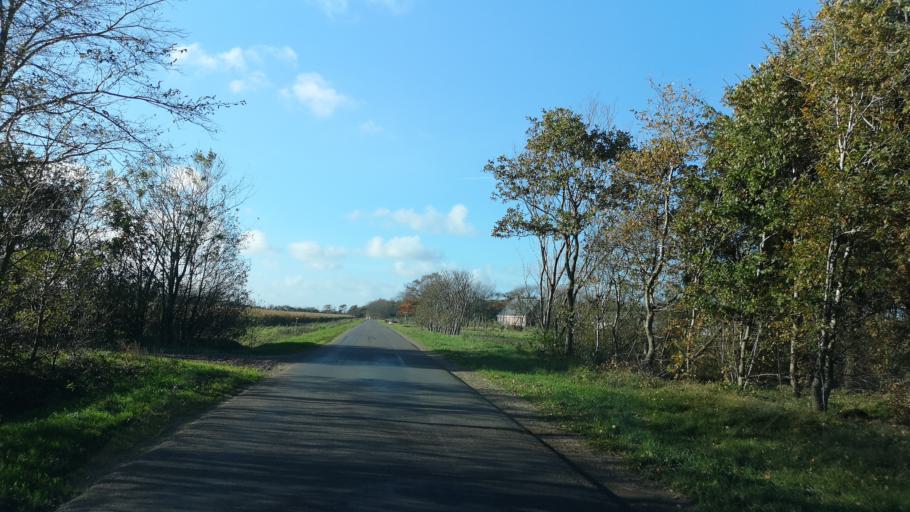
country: DK
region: Central Jutland
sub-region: Ringkobing-Skjern Kommune
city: Tarm
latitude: 55.8275
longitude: 8.3929
